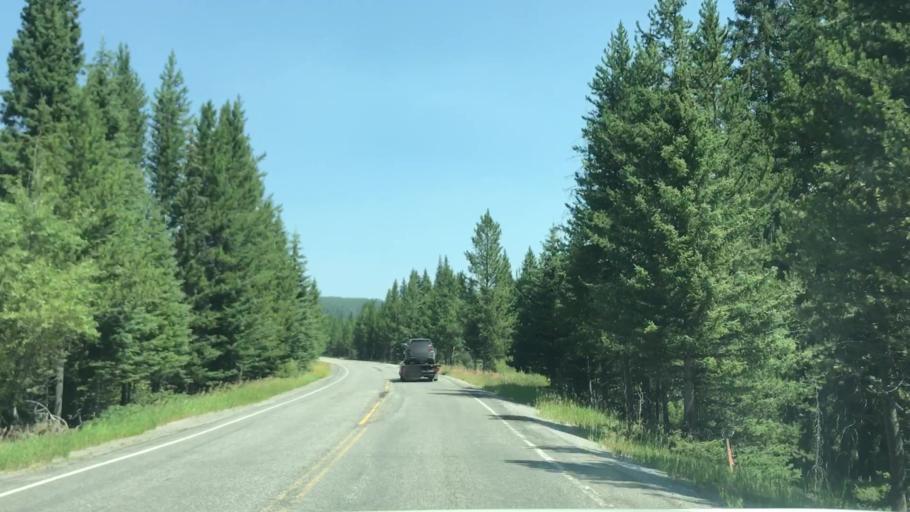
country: US
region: Montana
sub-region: Gallatin County
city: West Yellowstone
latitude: 44.8105
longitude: -111.0948
